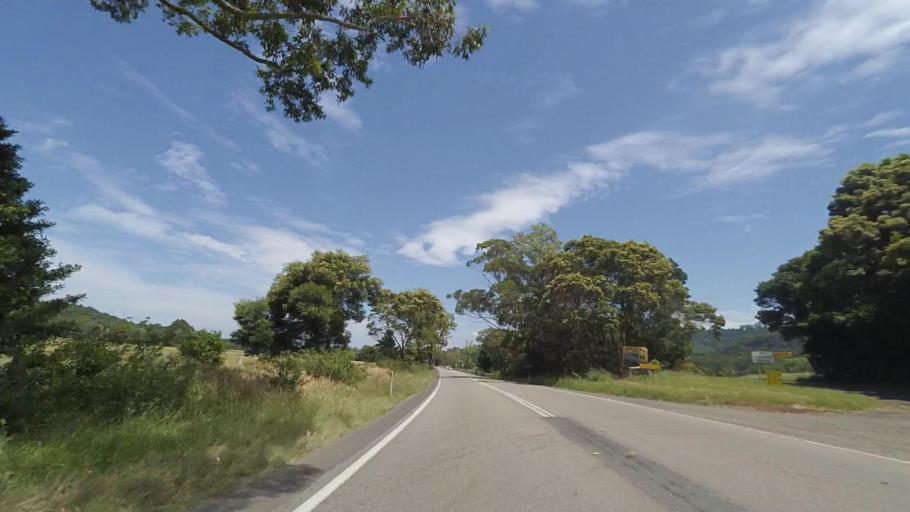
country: AU
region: New South Wales
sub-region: Kiama
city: Gerringong
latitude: -34.7406
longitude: 150.7636
